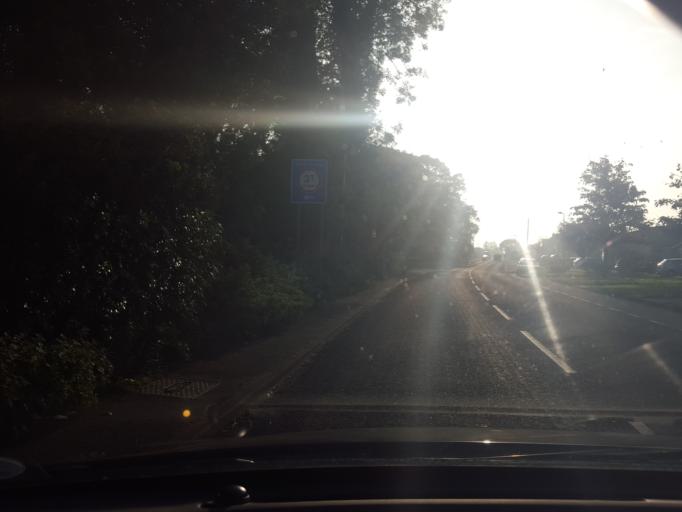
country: GB
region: England
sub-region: Essex
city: Walton-on-the-Naze
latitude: 51.8427
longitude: 1.2563
